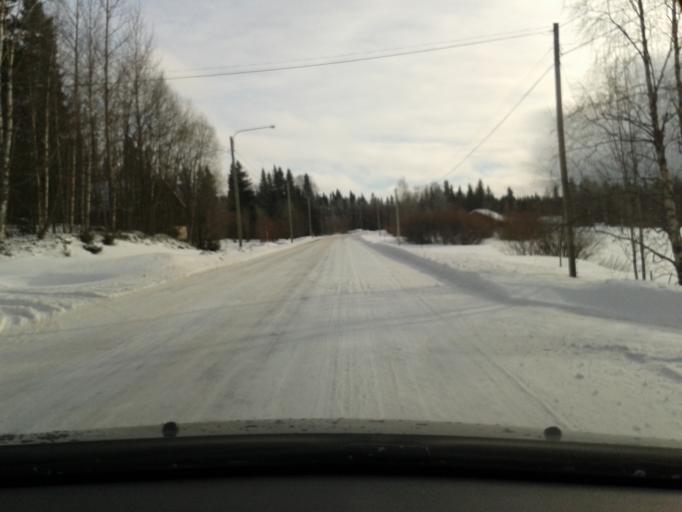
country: SE
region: Vaesterbotten
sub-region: Vilhelmina Kommun
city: Sjoberg
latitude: 64.6851
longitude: 16.2828
